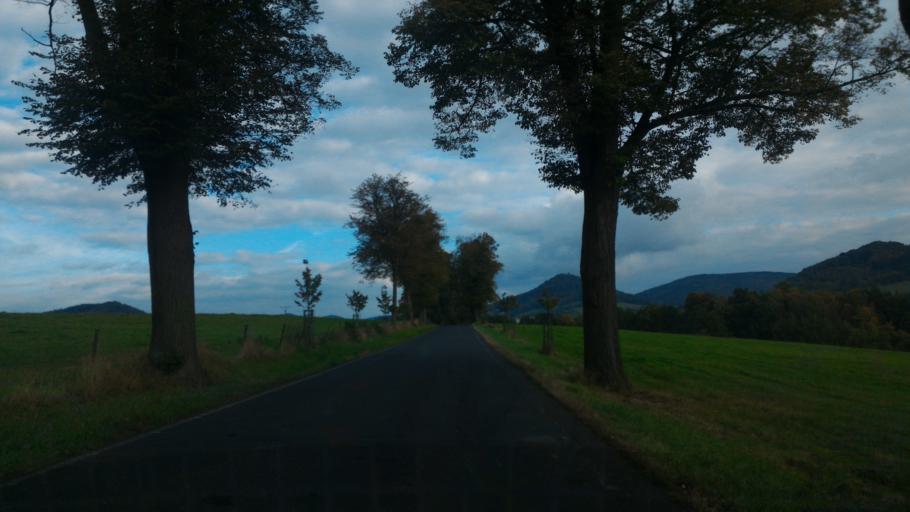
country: CZ
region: Ustecky
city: Ceska Kamenice
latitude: 50.8031
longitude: 14.3911
